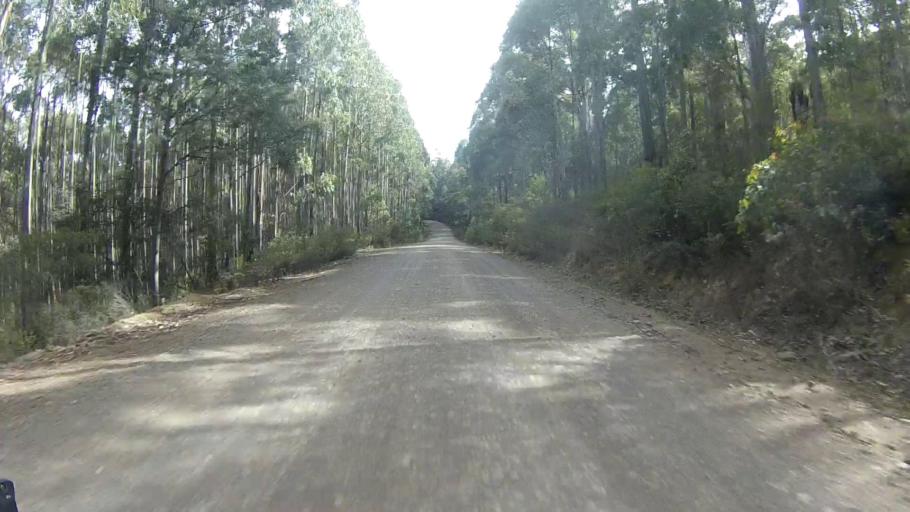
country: AU
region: Tasmania
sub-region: Sorell
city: Sorell
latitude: -42.7491
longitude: 147.8287
